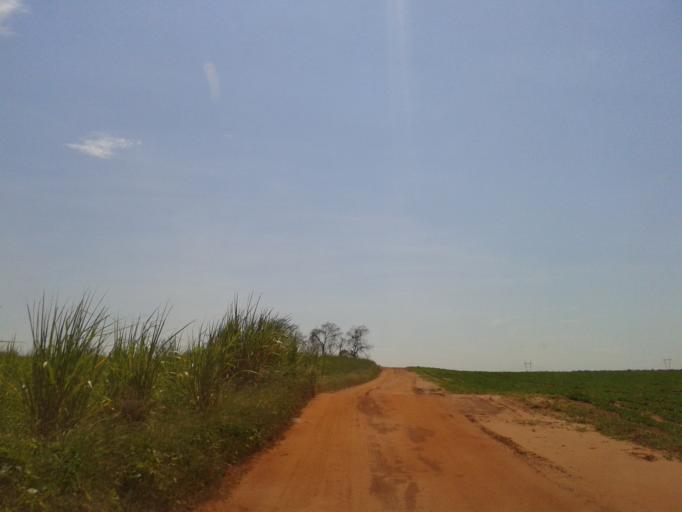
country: BR
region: Minas Gerais
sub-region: Santa Vitoria
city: Santa Vitoria
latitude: -19.0641
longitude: -50.4773
